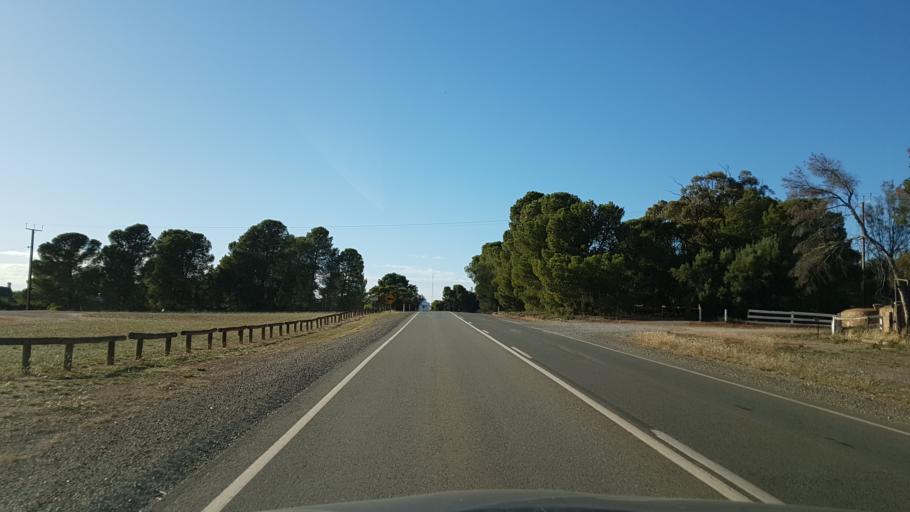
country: AU
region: South Australia
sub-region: Port Pirie City and Dists
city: Crystal Brook
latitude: -33.2689
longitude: 138.3503
